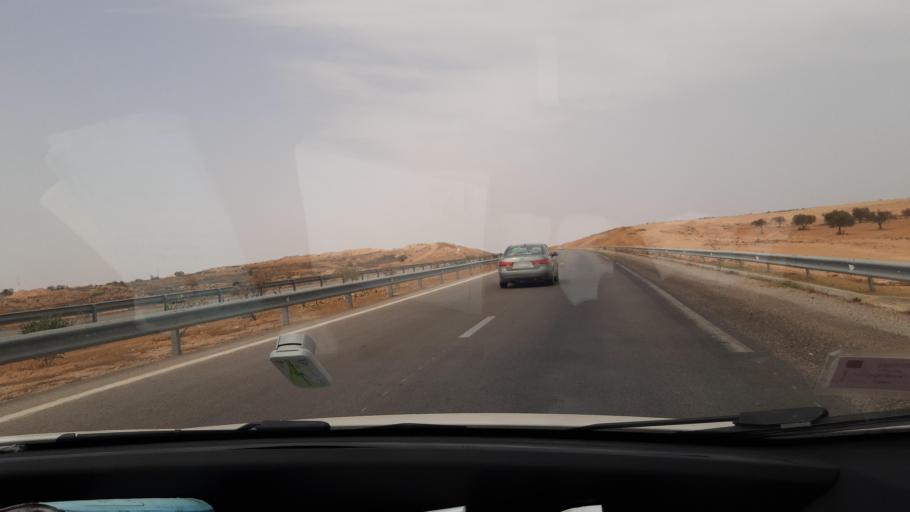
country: TN
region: Safaqis
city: Sfax
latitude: 34.7543
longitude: 10.6062
